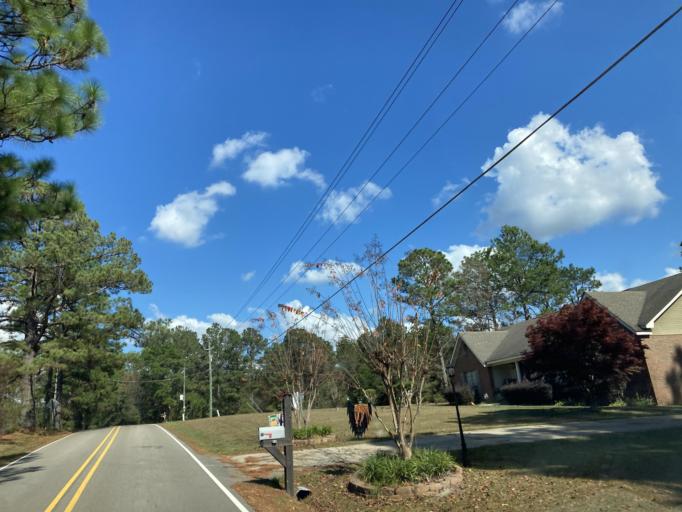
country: US
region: Mississippi
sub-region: Lamar County
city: West Hattiesburg
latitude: 31.2681
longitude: -89.3835
